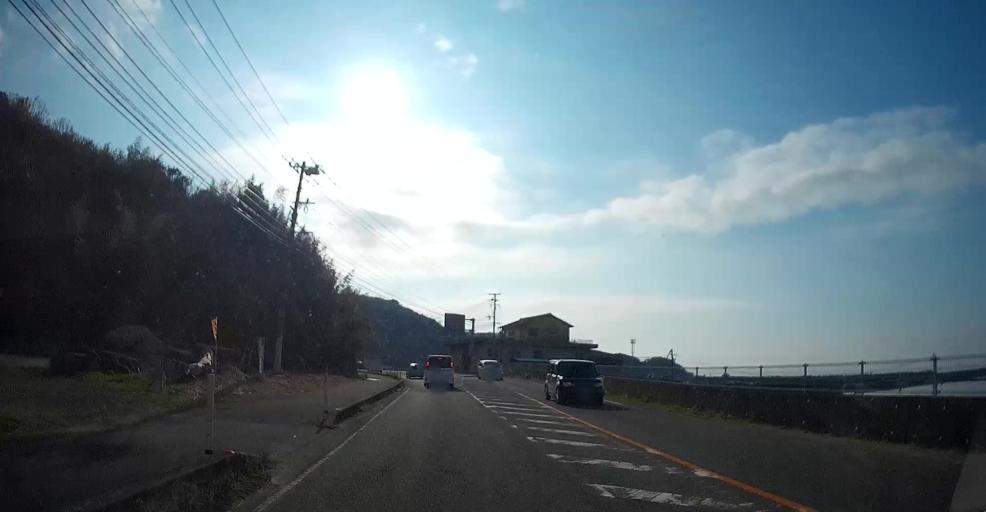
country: JP
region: Kumamoto
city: Yatsushiro
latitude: 32.5703
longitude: 130.4158
